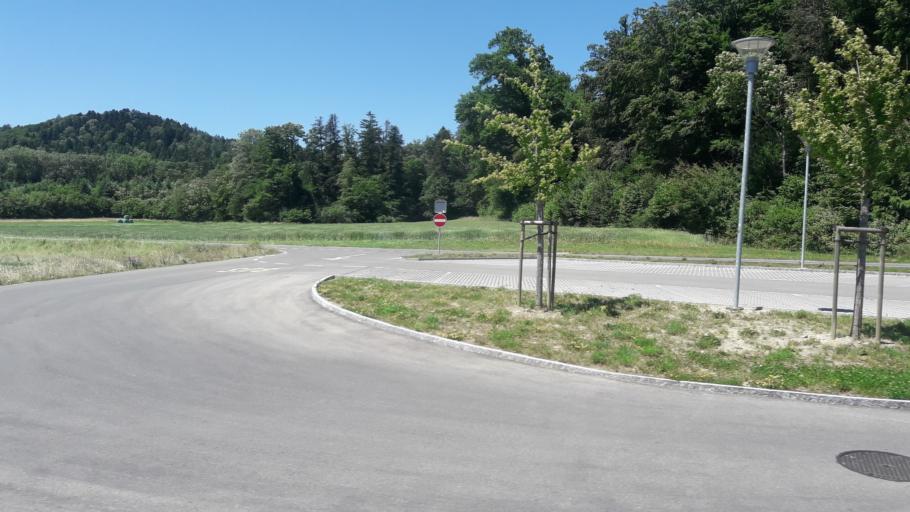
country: CH
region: Bern
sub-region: Seeland District
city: Tauffelen
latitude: 47.0473
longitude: 7.1772
